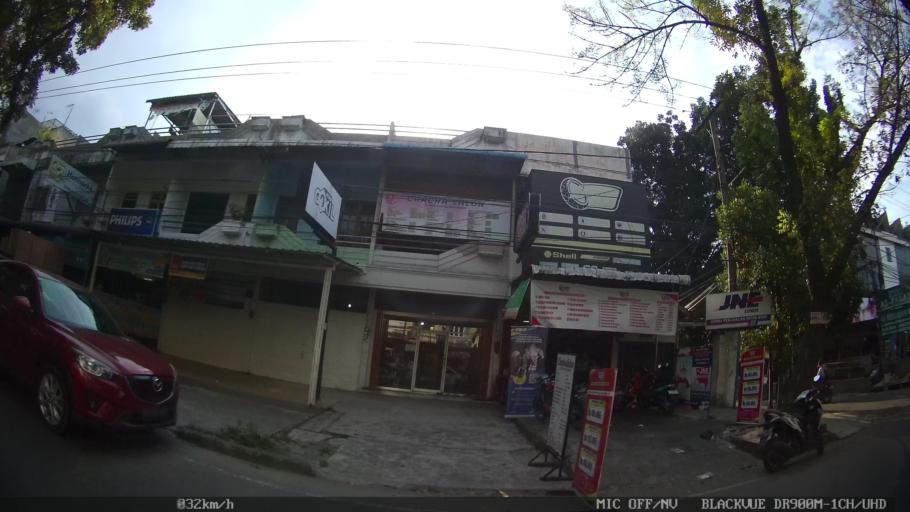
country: ID
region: North Sumatra
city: Medan
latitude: 3.5751
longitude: 98.6427
